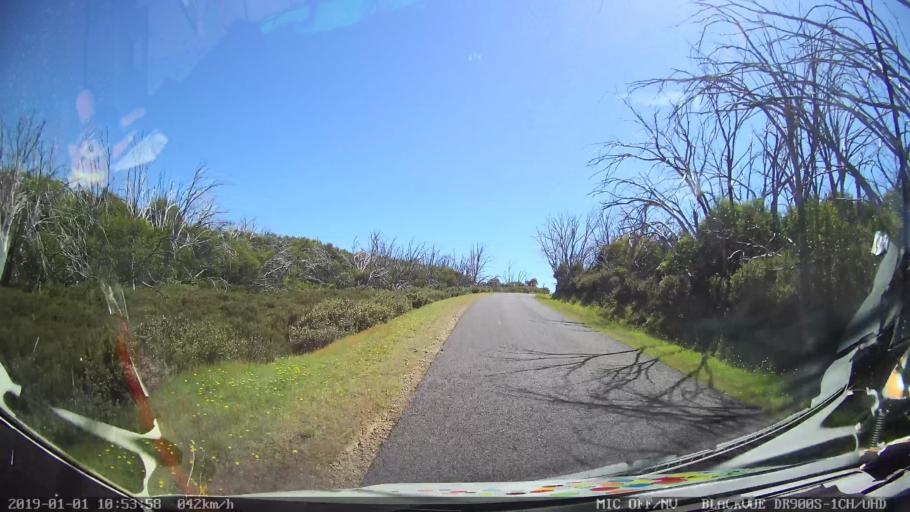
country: AU
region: New South Wales
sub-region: Snowy River
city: Jindabyne
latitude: -36.0111
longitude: 148.3820
